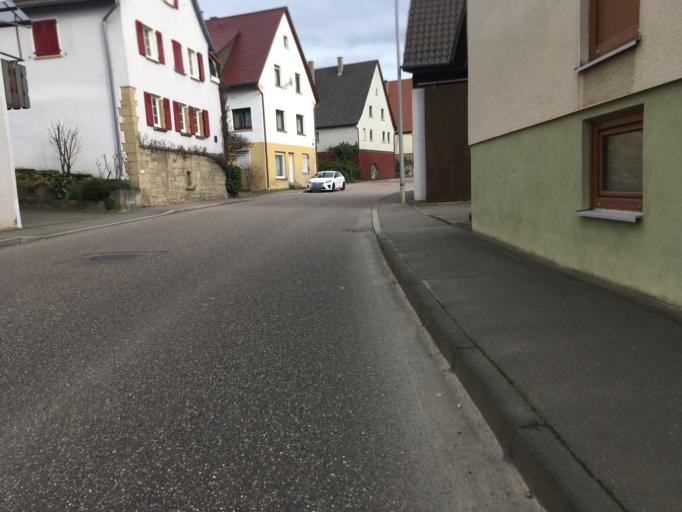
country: DE
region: Baden-Wuerttemberg
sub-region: Regierungsbezirk Stuttgart
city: Bretzfeld
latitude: 49.2143
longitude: 9.4108
